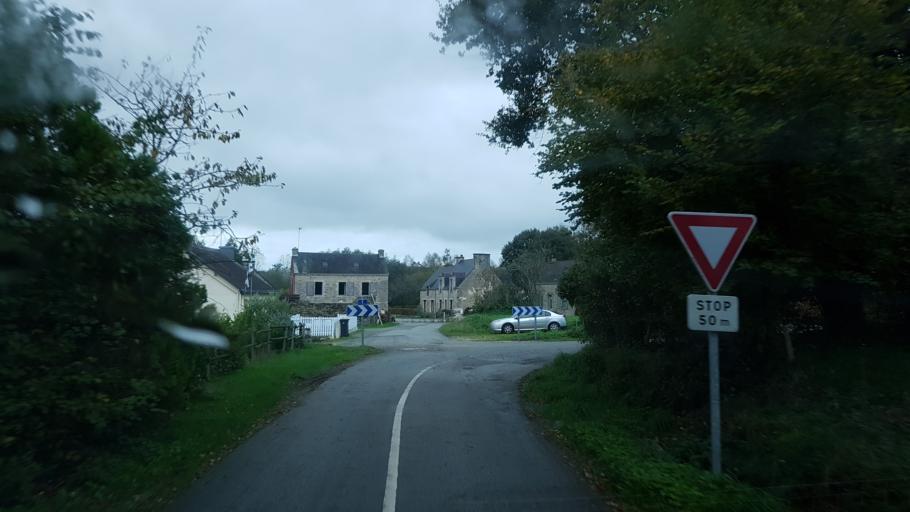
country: FR
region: Brittany
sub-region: Departement du Morbihan
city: Elven
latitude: 47.7458
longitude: -2.5647
